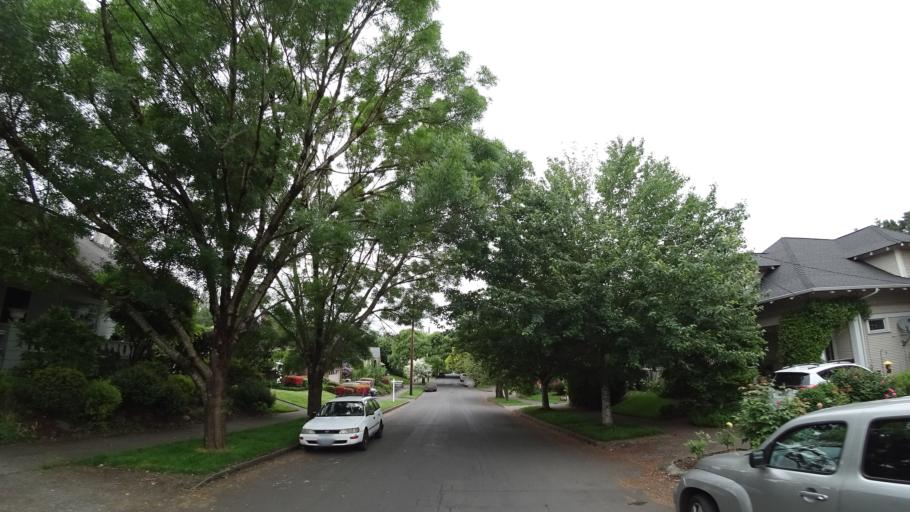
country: US
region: Oregon
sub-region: Multnomah County
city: Portland
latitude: 45.5019
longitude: -122.6360
